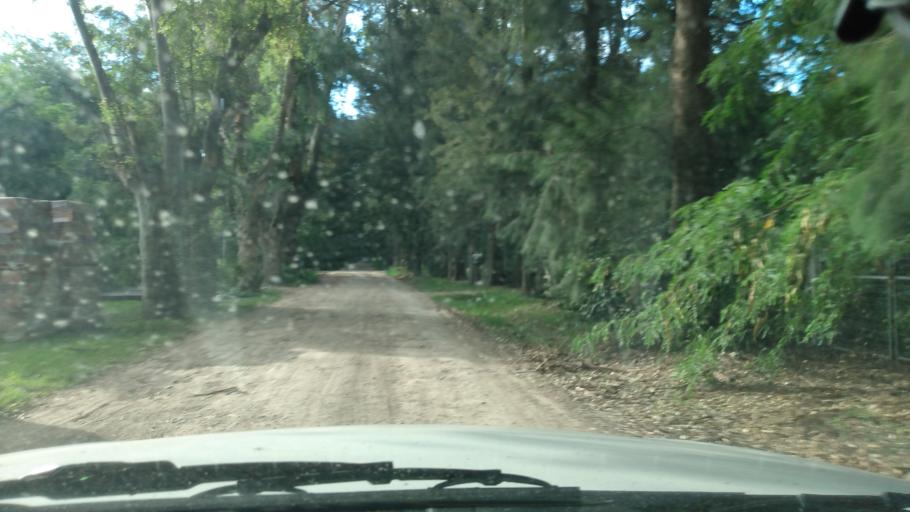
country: AR
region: Buenos Aires
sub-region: Partido de Lujan
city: Lujan
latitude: -34.5521
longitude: -59.1588
